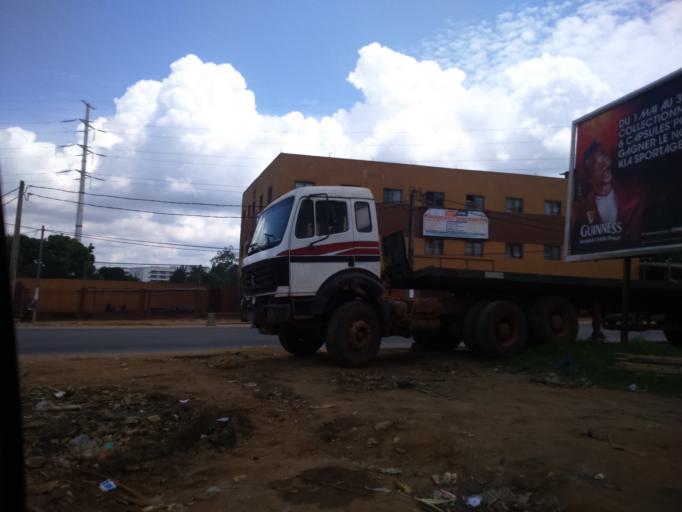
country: CI
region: Lagunes
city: Abidjan
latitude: 5.3584
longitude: -4.0851
